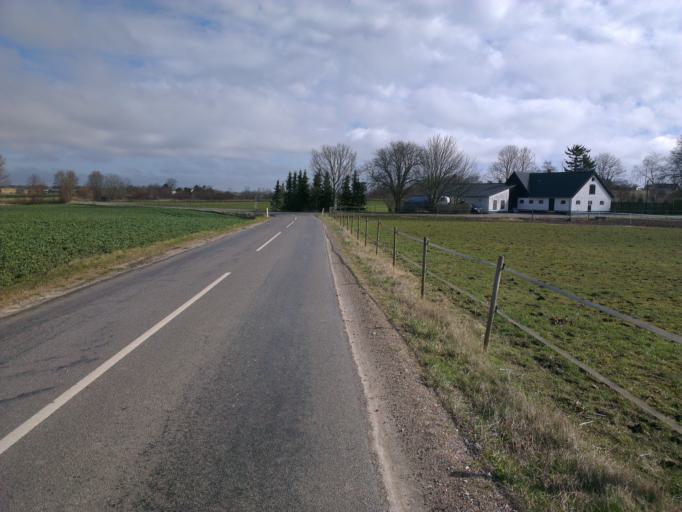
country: DK
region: Capital Region
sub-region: Hillerod Kommune
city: Skaevinge
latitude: 55.8719
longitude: 12.1161
